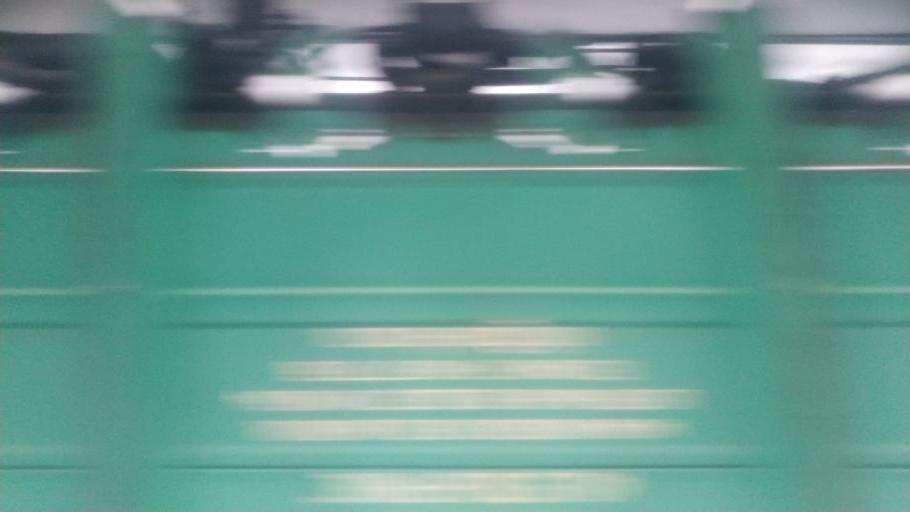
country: RU
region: Bashkortostan
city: Yanaul
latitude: 56.2734
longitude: 54.9331
